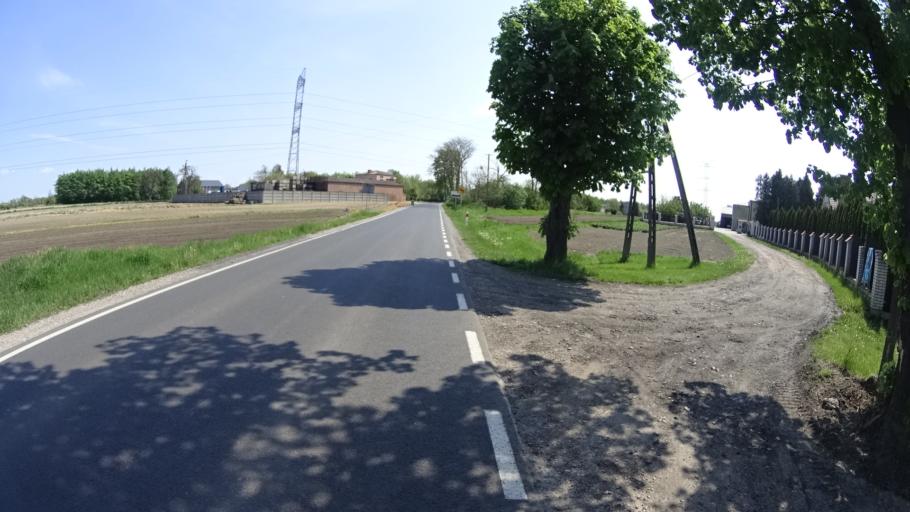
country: PL
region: Masovian Voivodeship
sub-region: Powiat warszawski zachodni
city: Ozarow Mazowiecki
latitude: 52.2337
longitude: 20.7598
